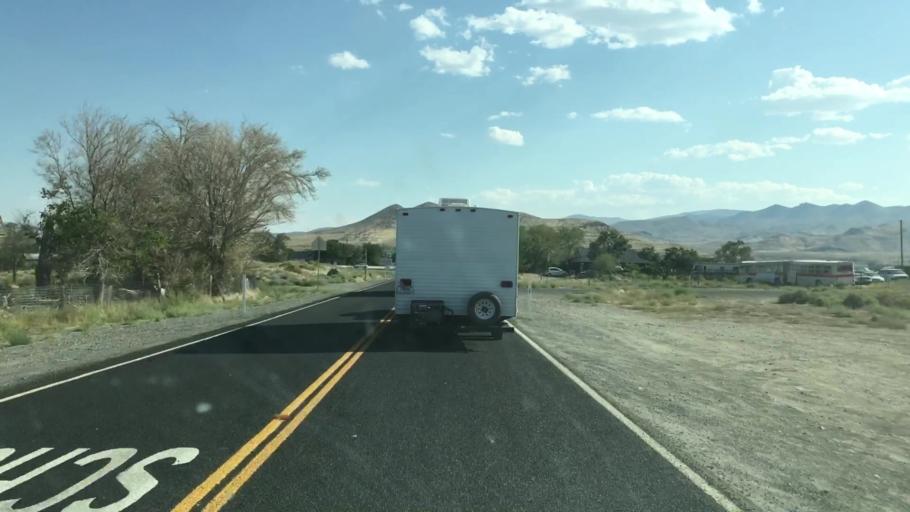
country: US
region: Nevada
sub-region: Lyon County
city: Fernley
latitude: 39.6332
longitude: -119.2906
